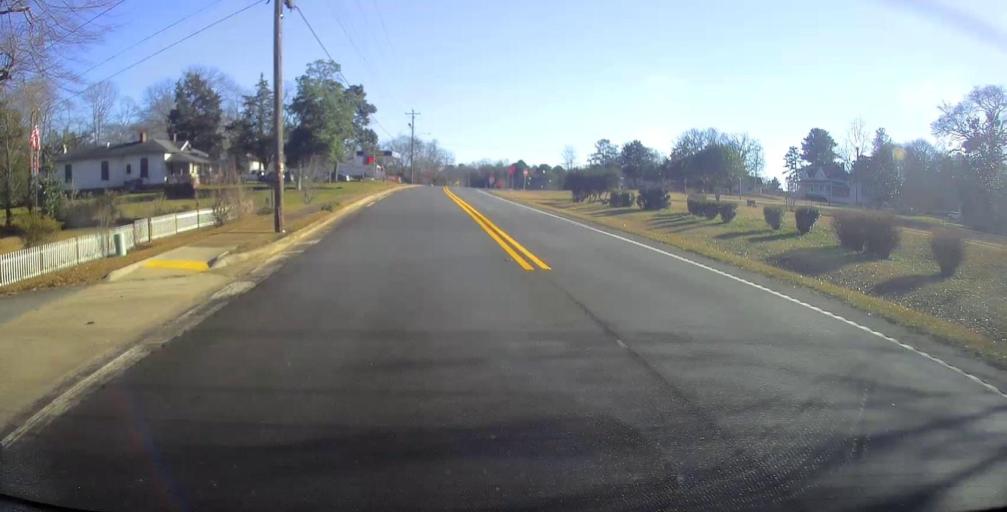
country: US
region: Georgia
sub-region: Talbot County
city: Sardis
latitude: 32.8083
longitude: -84.6961
